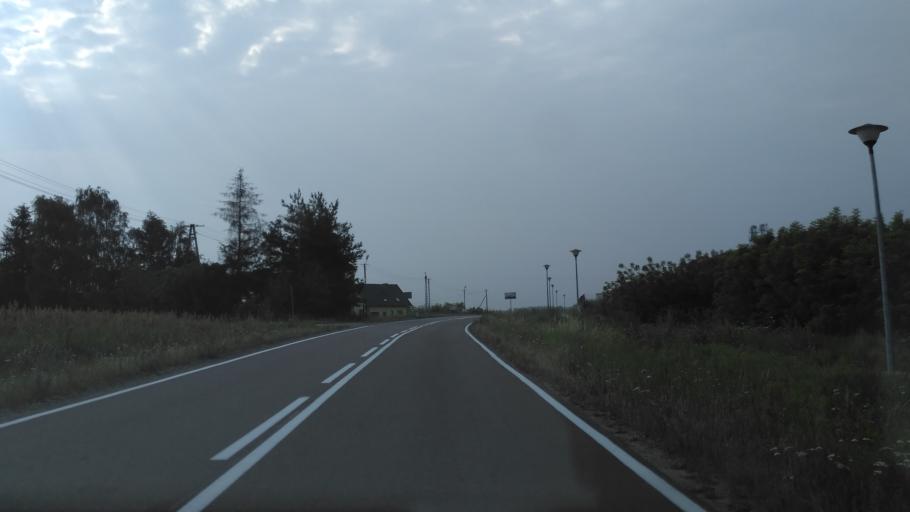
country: PL
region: Lublin Voivodeship
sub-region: Powiat chelmski
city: Rejowiec Fabryczny
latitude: 51.1853
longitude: 23.1715
